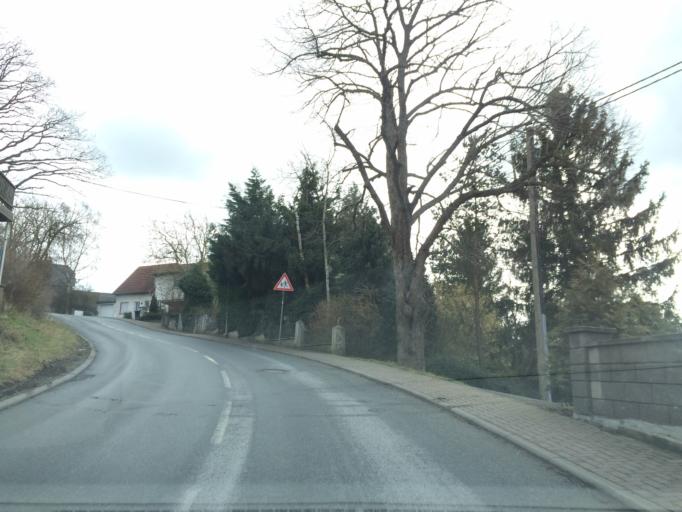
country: DE
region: Hesse
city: Weilmunster
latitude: 50.3809
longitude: 8.4012
